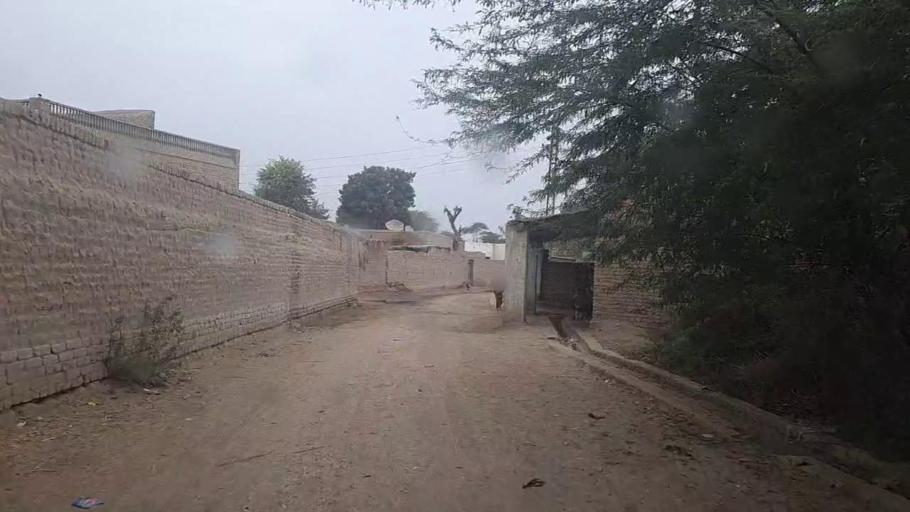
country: PK
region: Sindh
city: Gambat
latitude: 27.3584
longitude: 68.5976
